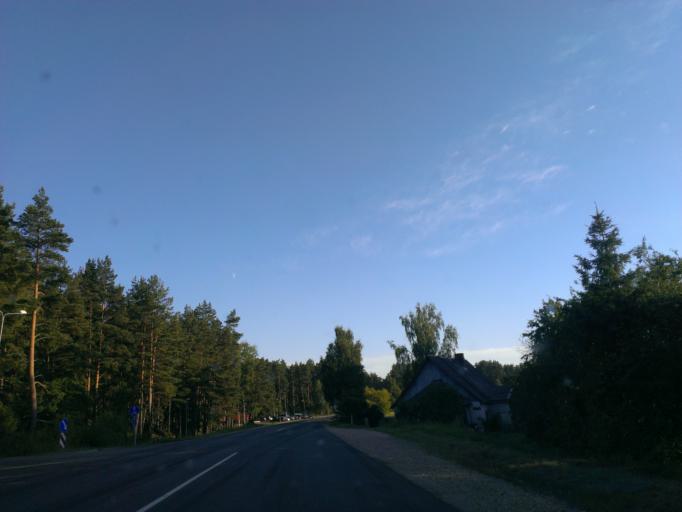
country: LV
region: Adazi
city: Adazi
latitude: 57.0639
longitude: 24.3236
